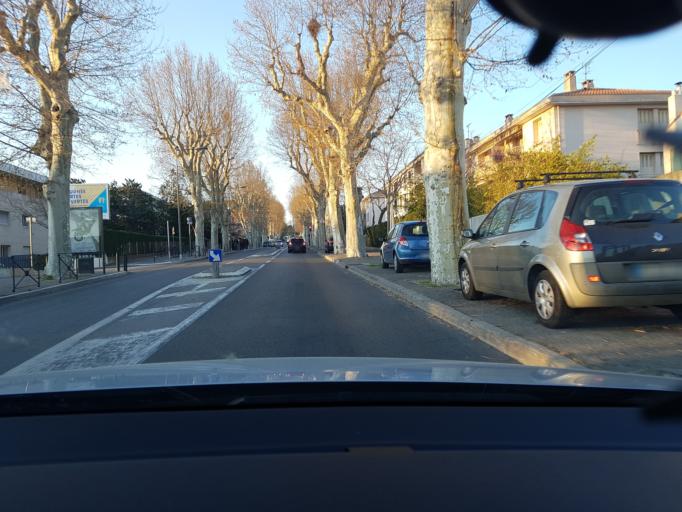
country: FR
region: Provence-Alpes-Cote d'Azur
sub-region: Departement des Bouches-du-Rhone
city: Aix-en-Provence
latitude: 43.5140
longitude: 5.4426
